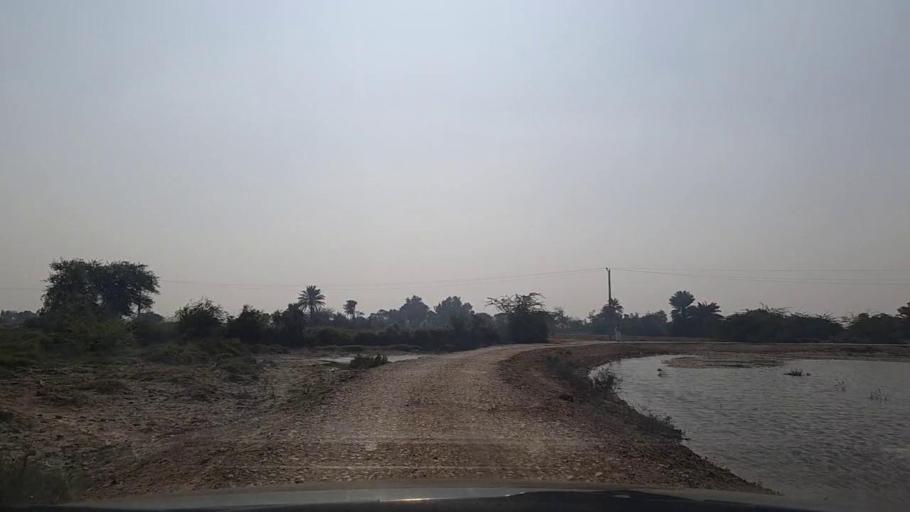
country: PK
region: Sindh
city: Mirpur Sakro
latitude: 24.5632
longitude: 67.7761
